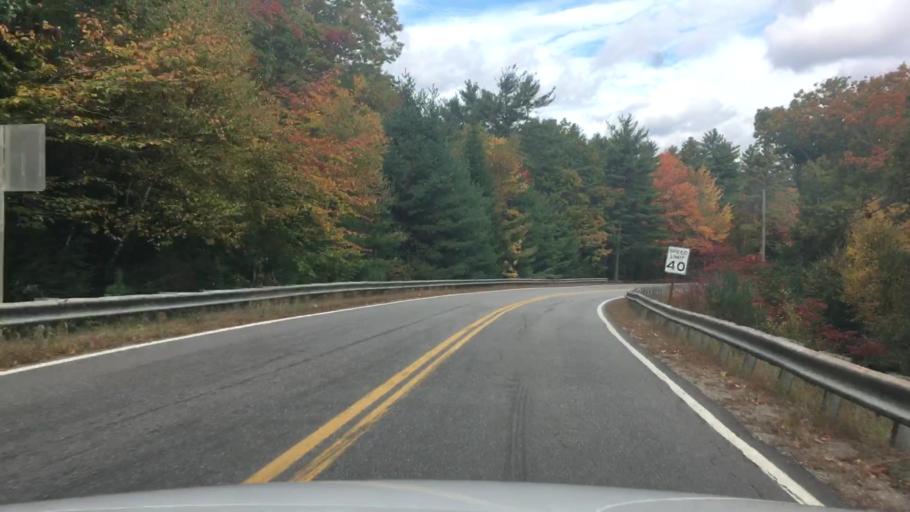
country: US
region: Maine
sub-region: Knox County
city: Hope
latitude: 44.2620
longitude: -69.1341
